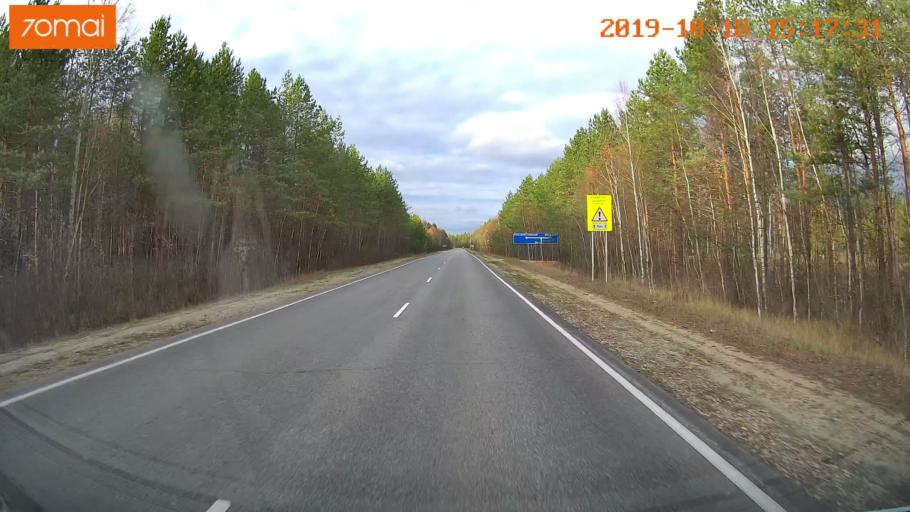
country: RU
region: Vladimir
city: Anopino
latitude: 55.6509
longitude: 40.7267
